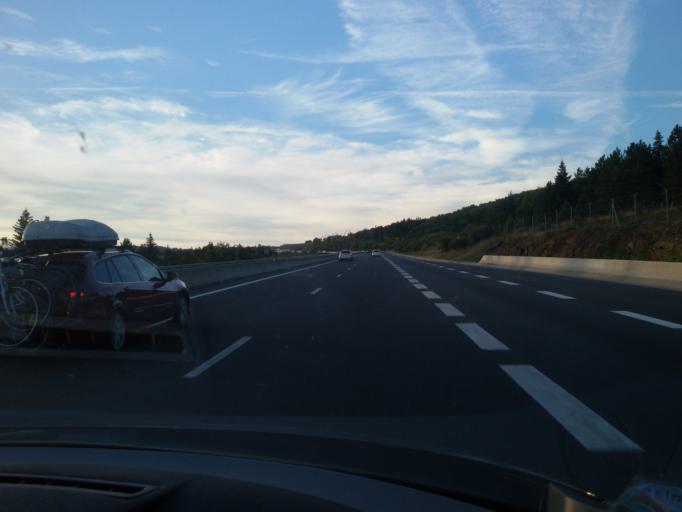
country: FR
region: Midi-Pyrenees
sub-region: Departement de l'Aveyron
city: Severac-le-Chateau
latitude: 44.2232
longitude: 3.0710
